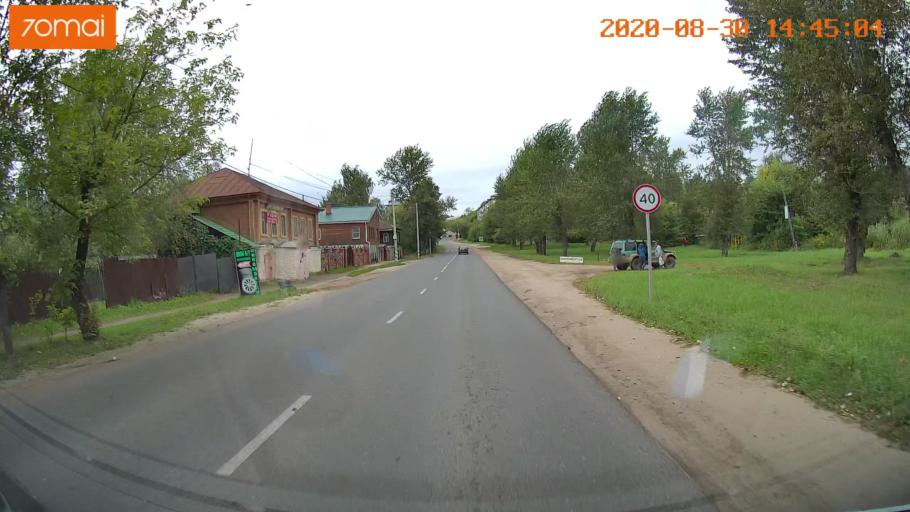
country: RU
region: Ivanovo
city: Kineshma
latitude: 57.4422
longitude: 42.1570
